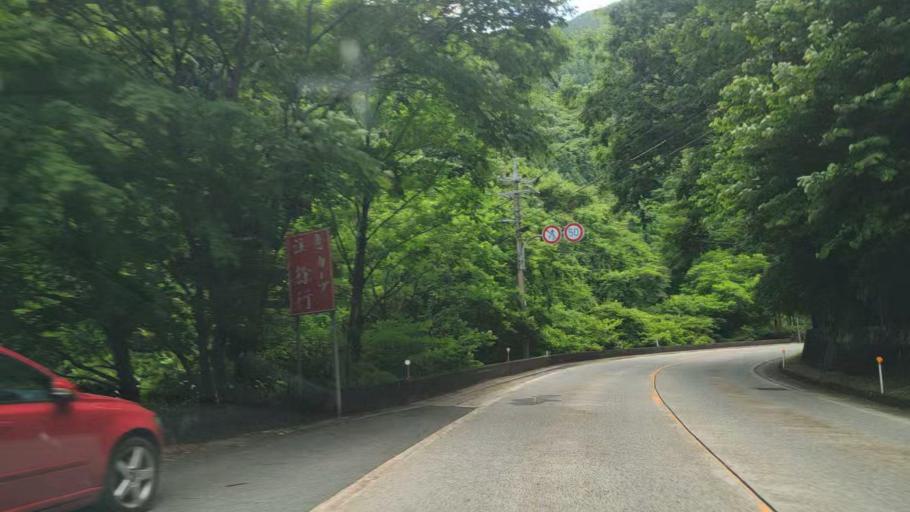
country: JP
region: Okayama
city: Niimi
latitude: 35.2141
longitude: 133.4806
